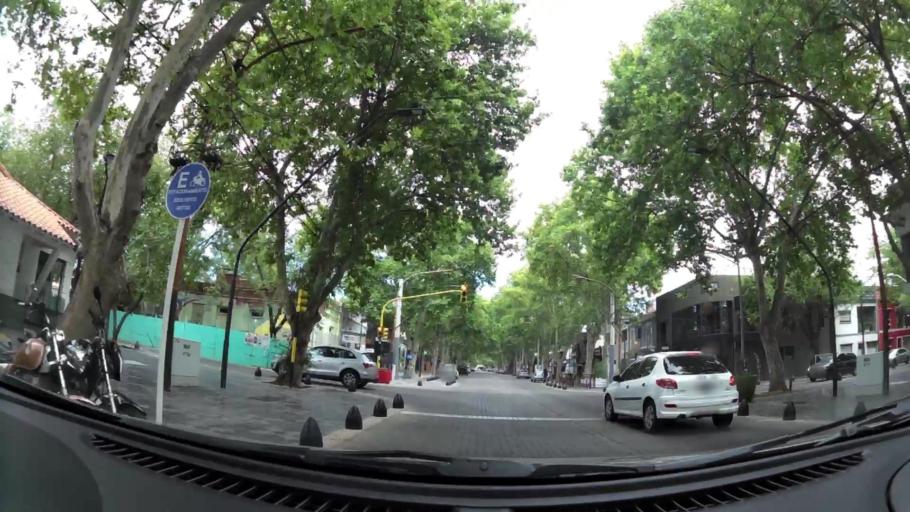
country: AR
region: Mendoza
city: Mendoza
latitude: -32.8920
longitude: -68.8566
